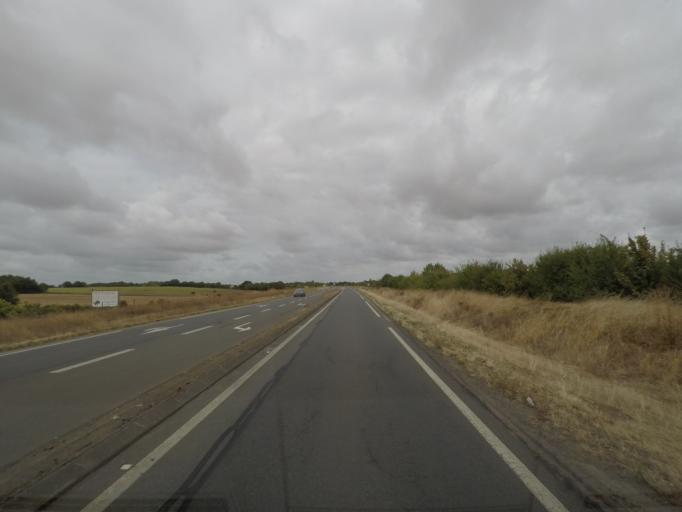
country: FR
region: Poitou-Charentes
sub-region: Departement des Deux-Sevres
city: Thorigne
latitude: 46.2844
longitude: -0.2638
